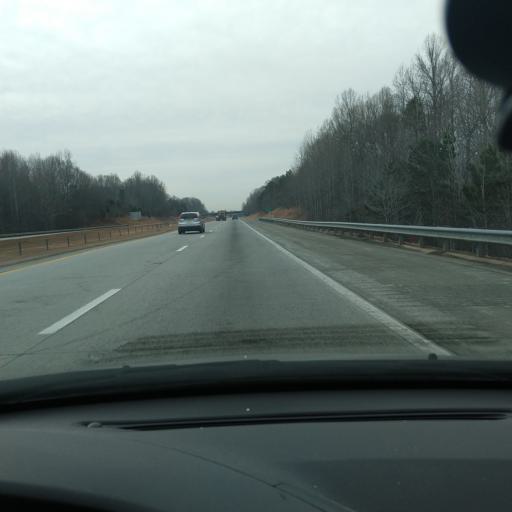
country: US
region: North Carolina
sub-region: Davidson County
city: Lexington
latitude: 35.8244
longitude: -80.2842
